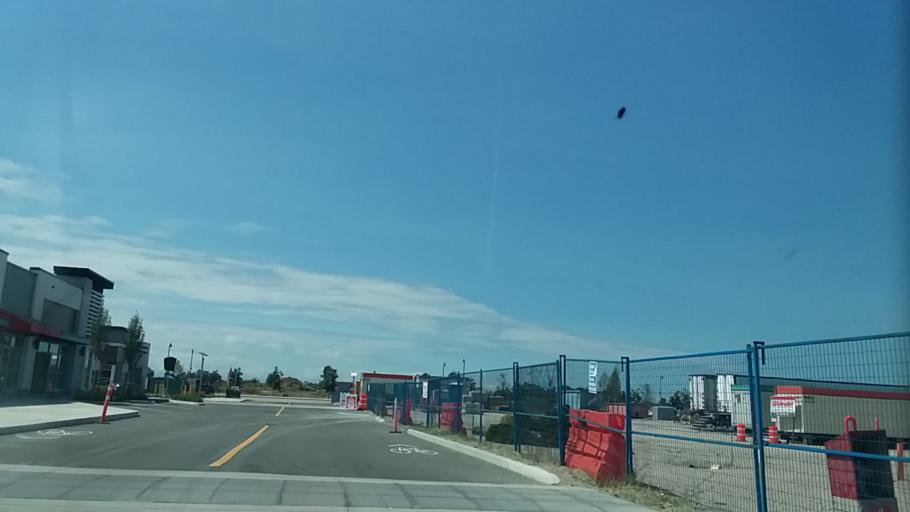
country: CA
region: British Columbia
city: Ladner
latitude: 49.0412
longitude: -123.0884
